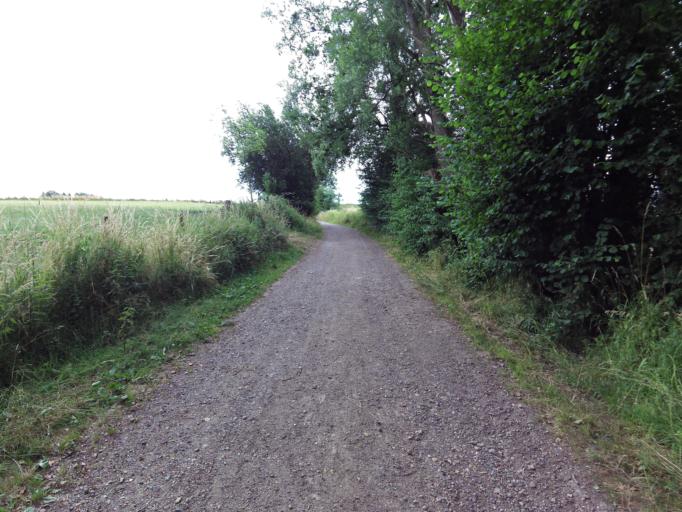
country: NL
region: Limburg
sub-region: Gemeente Simpelveld
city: Simpelveld
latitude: 50.7969
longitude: 5.9410
